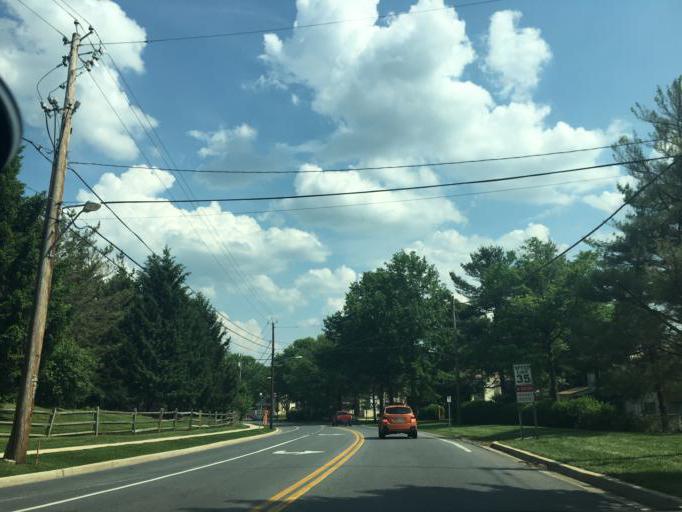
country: US
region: Maryland
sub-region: Montgomery County
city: Montgomery Village
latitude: 39.1902
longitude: -77.1917
